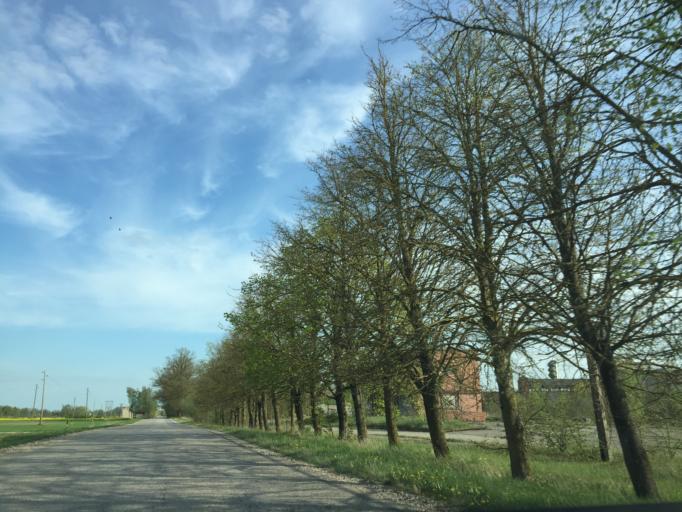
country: LV
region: Bauskas Rajons
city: Bauska
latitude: 56.3396
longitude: 24.2371
